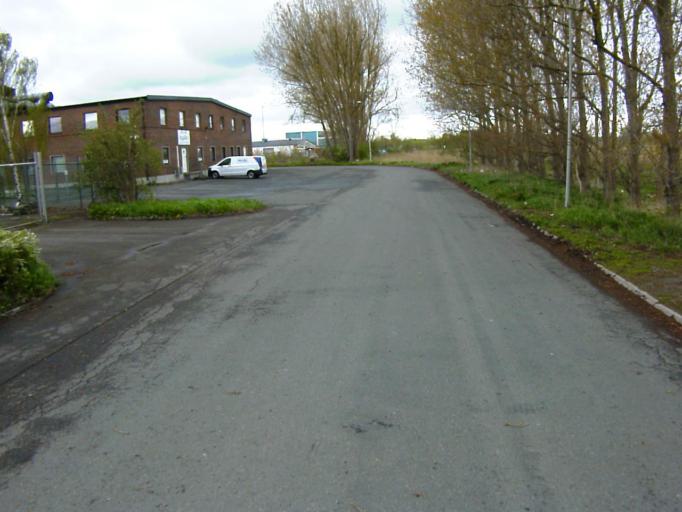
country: SE
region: Skane
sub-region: Kristianstads Kommun
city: Kristianstad
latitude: 56.0240
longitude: 14.1375
